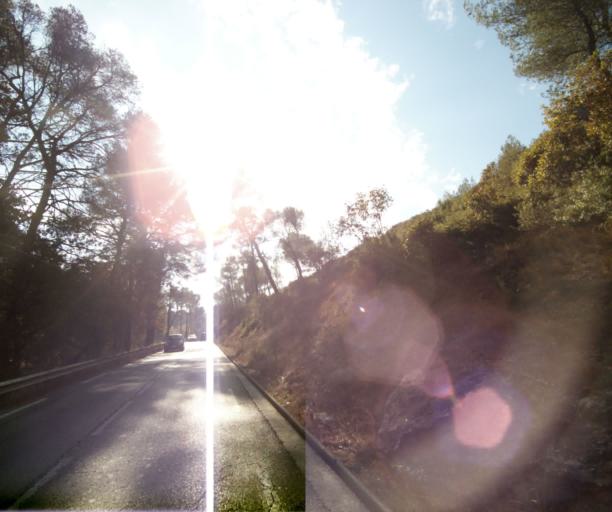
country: FR
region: Provence-Alpes-Cote d'Azur
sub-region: Departement des Bouches-du-Rhone
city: Allauch
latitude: 43.3147
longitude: 5.4980
